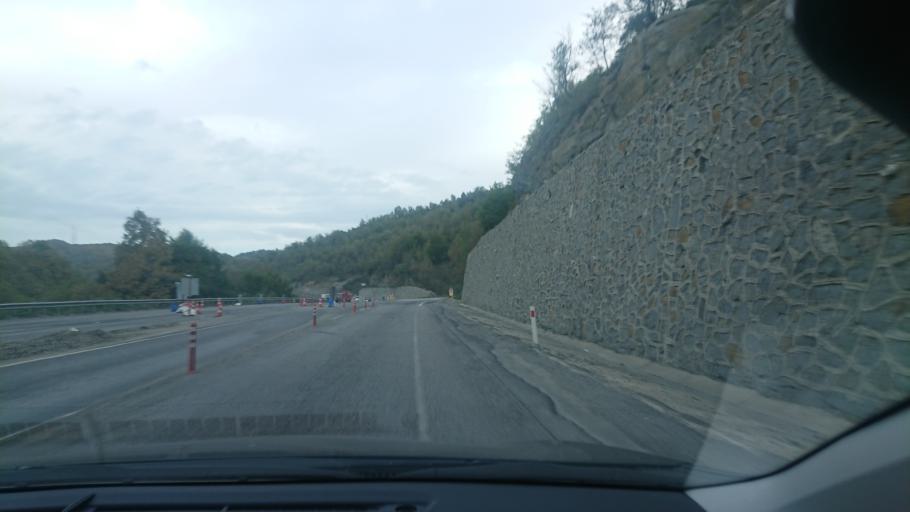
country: TR
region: Zonguldak
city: Beycuma
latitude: 41.4028
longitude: 31.9372
